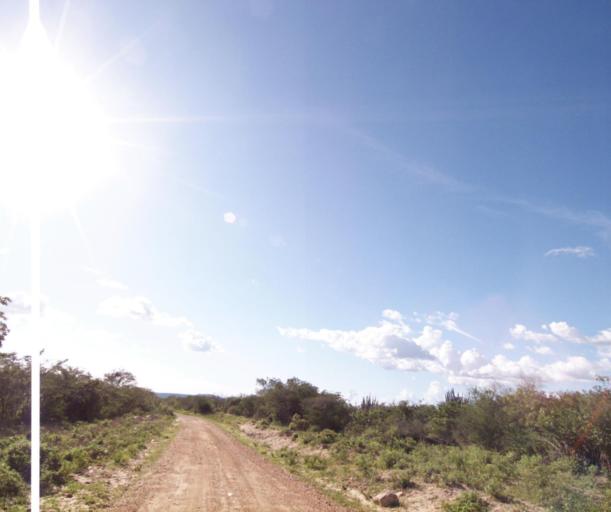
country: BR
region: Bahia
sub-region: Tanhacu
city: Tanhacu
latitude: -14.1891
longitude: -40.9746
